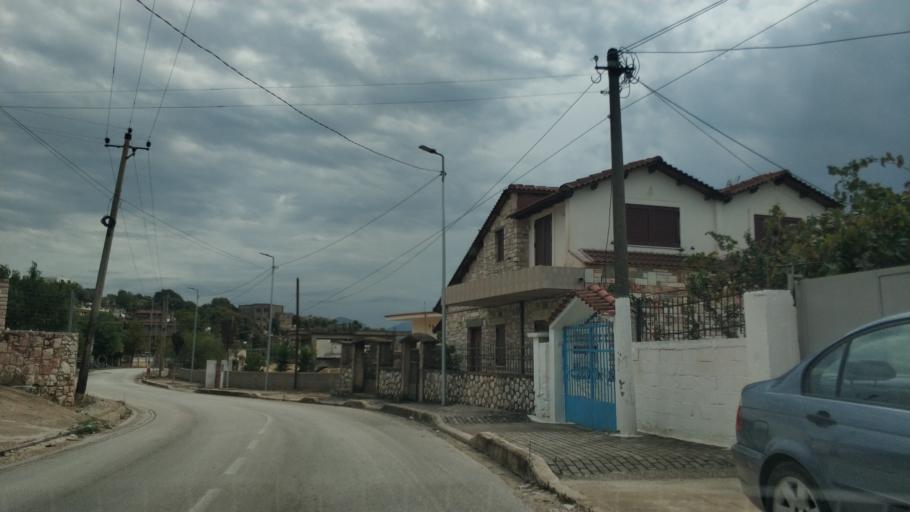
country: AL
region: Vlore
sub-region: Rrethi i Sarandes
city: Sarande
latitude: 39.8469
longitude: 20.0313
